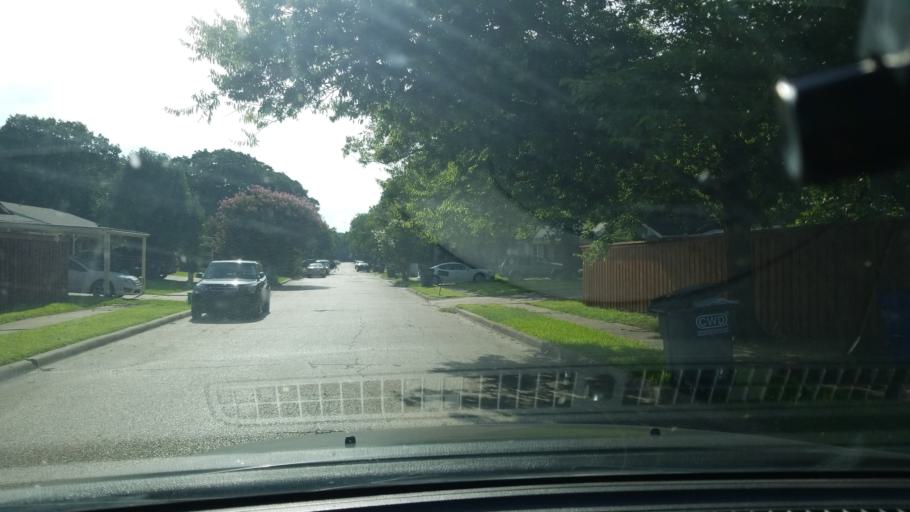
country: US
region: Texas
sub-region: Dallas County
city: Balch Springs
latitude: 32.7181
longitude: -96.6310
